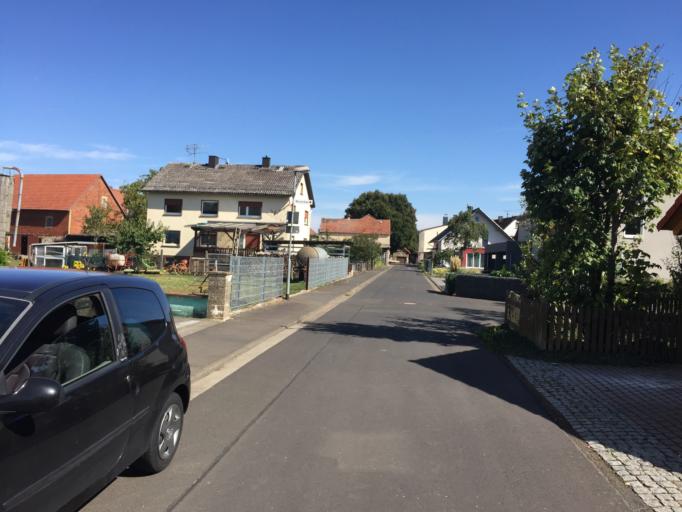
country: DE
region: Hesse
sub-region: Regierungsbezirk Giessen
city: Reiskirchen
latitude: 50.5940
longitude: 8.8528
